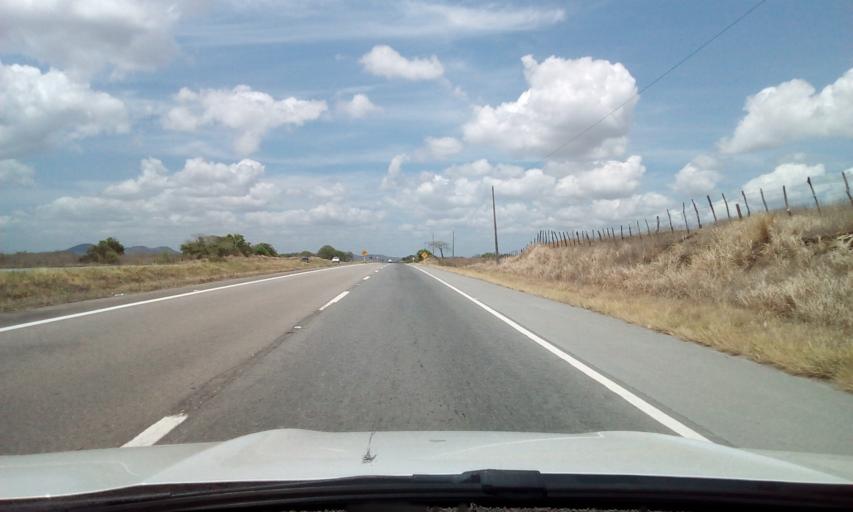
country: BR
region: Paraiba
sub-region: Pilar
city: Pilar
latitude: -7.1793
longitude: -35.3186
